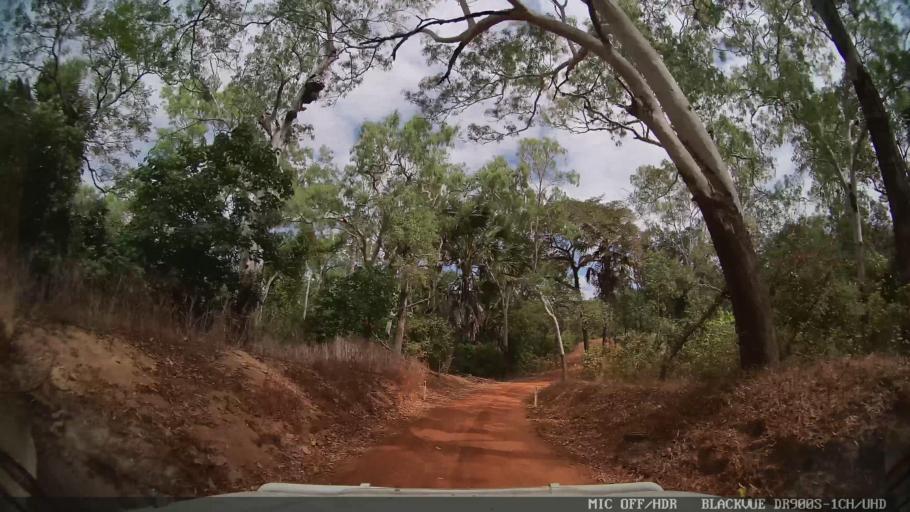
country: AU
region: Queensland
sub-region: Cook
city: Cooktown
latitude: -15.2919
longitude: 144.8438
